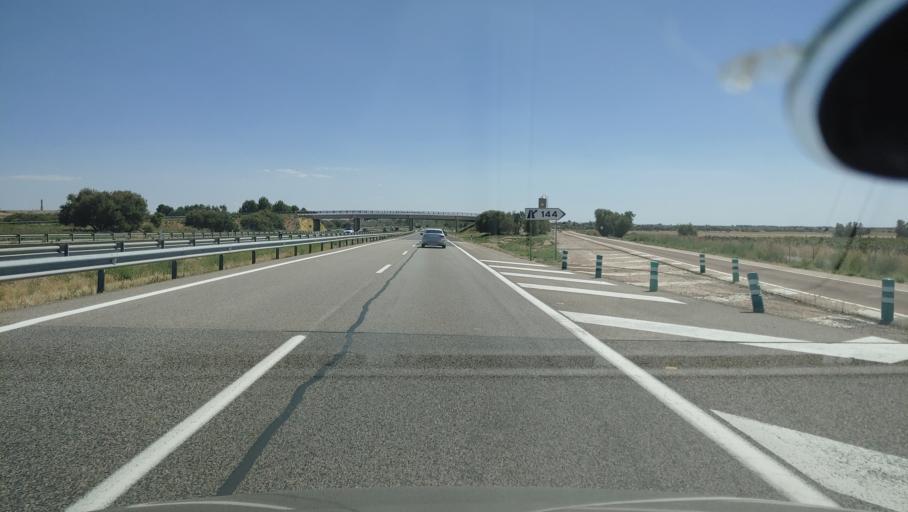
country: ES
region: Castille-La Mancha
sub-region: Provincia de Ciudad Real
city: Villarta de San Juan
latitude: 39.2544
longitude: -3.4342
